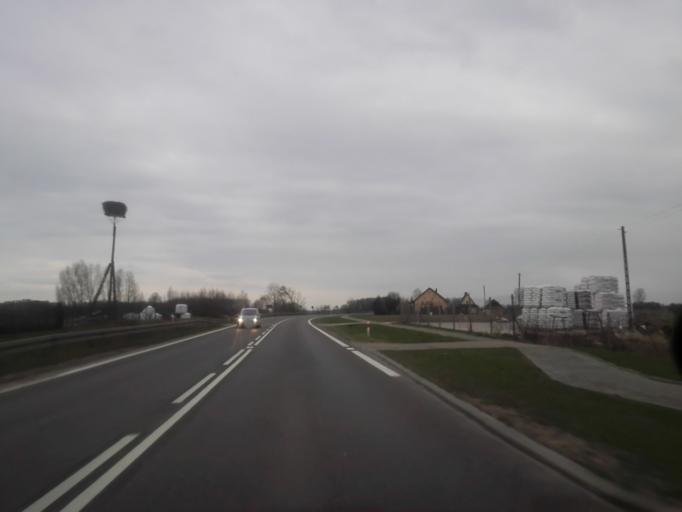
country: PL
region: Podlasie
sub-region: Powiat grajewski
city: Rajgrod
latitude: 53.6831
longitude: 22.6173
